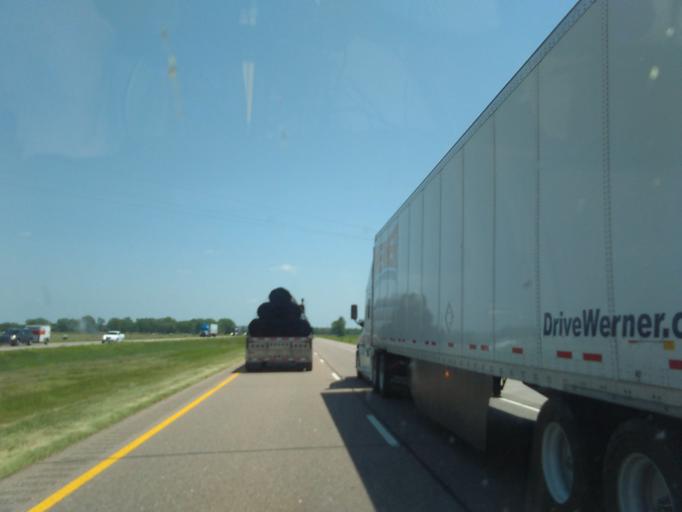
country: US
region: Nebraska
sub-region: Dawson County
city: Gothenburg
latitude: 40.8981
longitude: -100.1258
